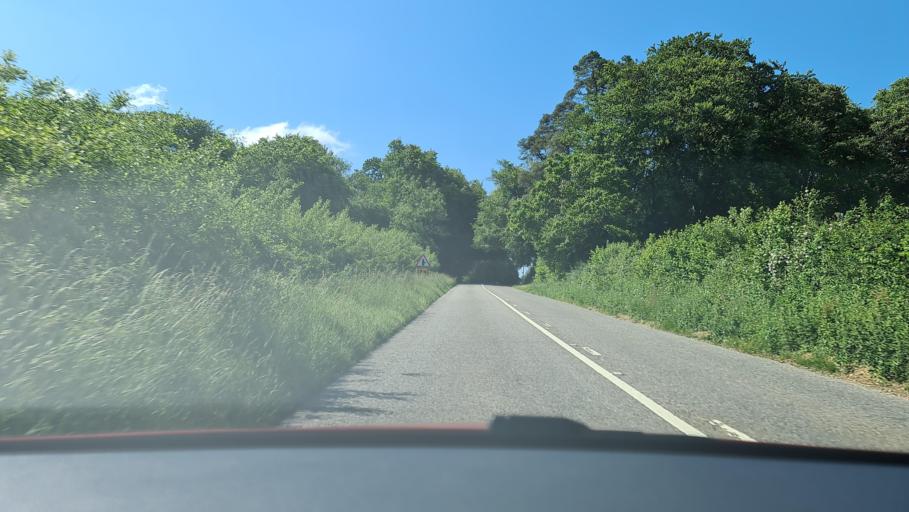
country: GB
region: England
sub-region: Cornwall
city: Lostwithiel
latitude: 50.4252
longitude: -4.6425
